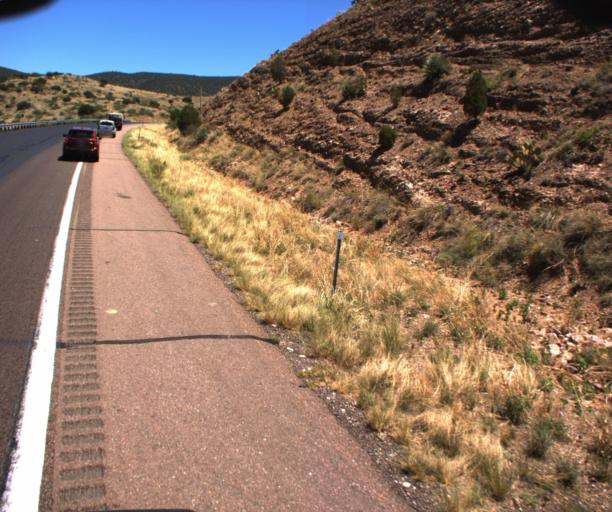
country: US
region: Arizona
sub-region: Gila County
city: Payson
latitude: 34.1379
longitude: -111.3294
